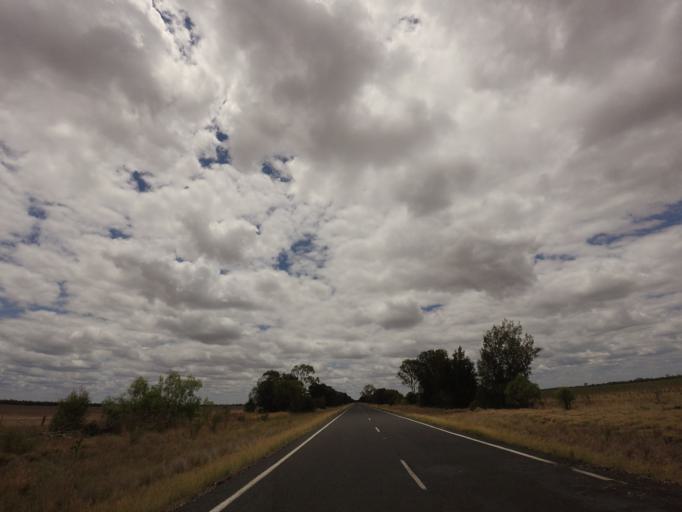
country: AU
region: Queensland
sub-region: Goondiwindi
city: Goondiwindi
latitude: -28.1679
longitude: 150.5200
